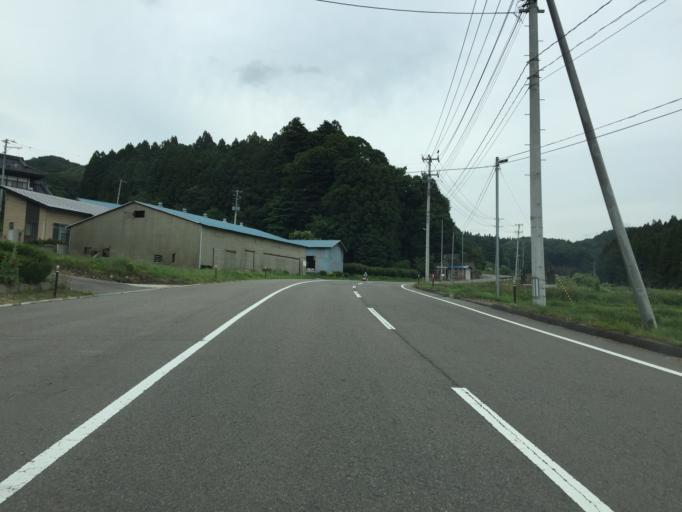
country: JP
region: Fukushima
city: Funehikimachi-funehiki
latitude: 37.4022
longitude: 140.6298
